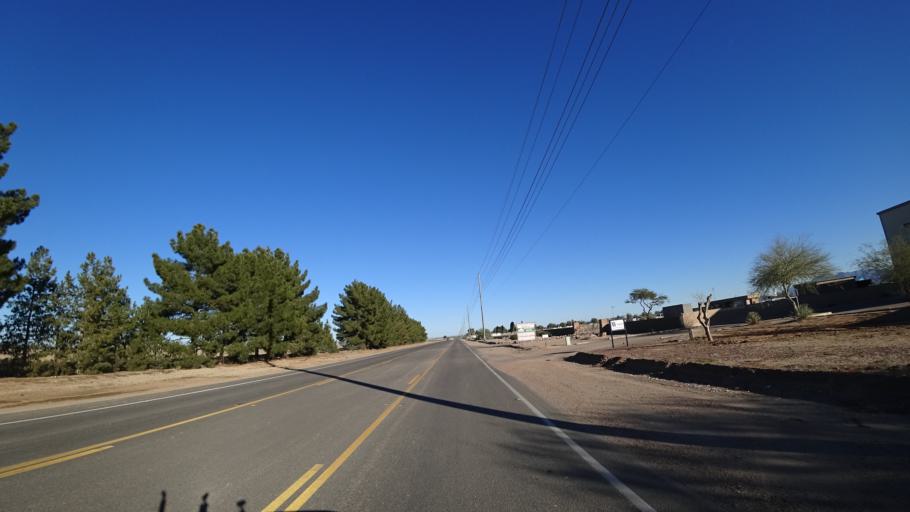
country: US
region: Arizona
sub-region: Maricopa County
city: Citrus Park
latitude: 33.4646
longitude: -112.4552
